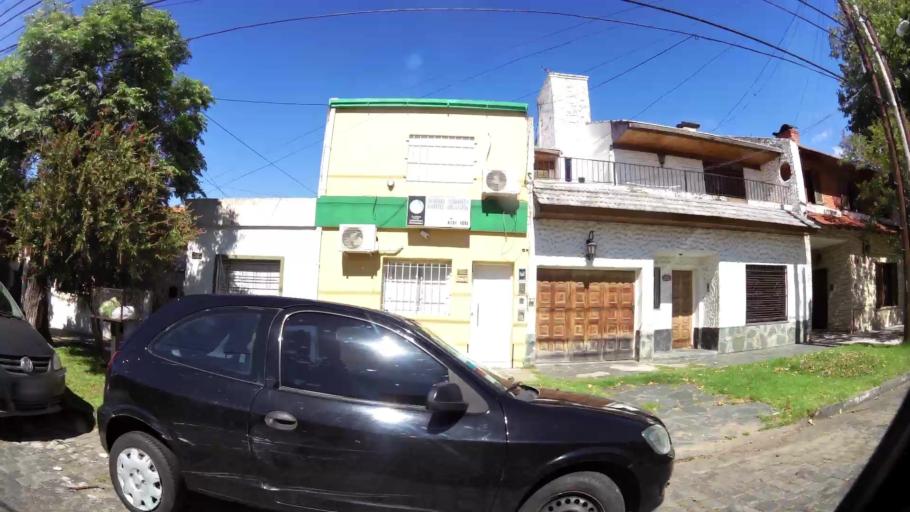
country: AR
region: Buenos Aires
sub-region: Partido de Lomas de Zamora
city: Lomas de Zamora
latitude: -34.7561
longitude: -58.4120
